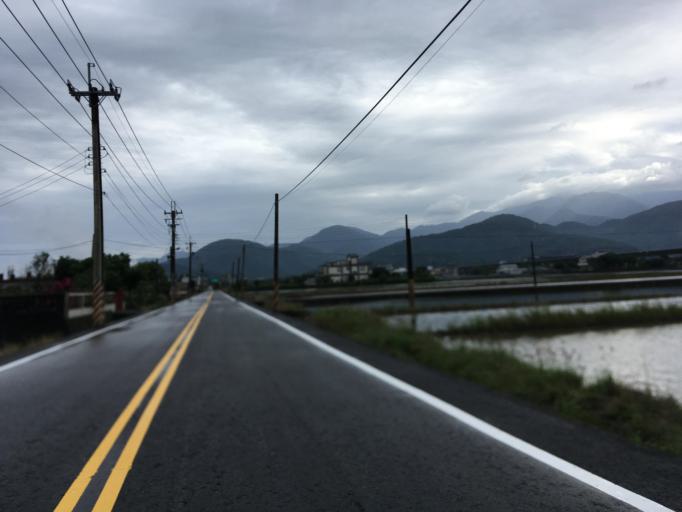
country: TW
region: Taiwan
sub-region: Yilan
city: Yilan
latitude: 24.6409
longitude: 121.8079
